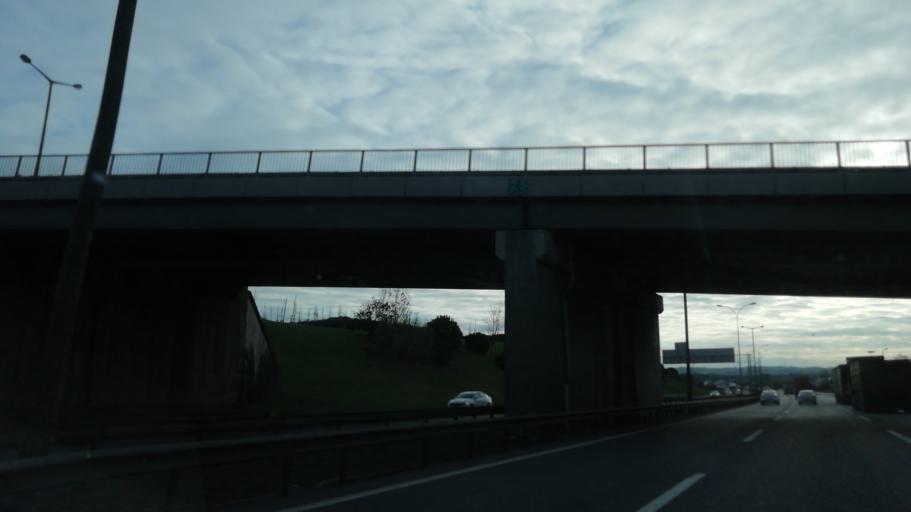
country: TR
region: Istanbul
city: Sultanbeyli
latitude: 40.9364
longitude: 29.3316
